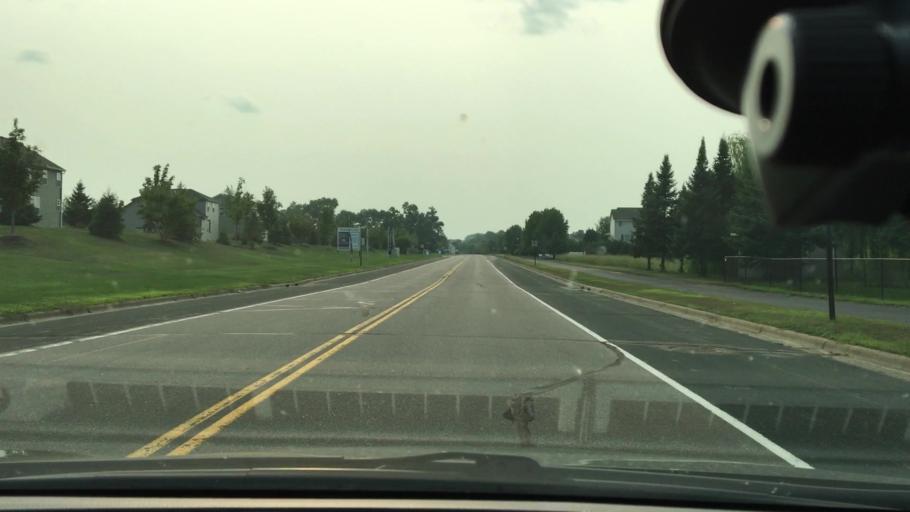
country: US
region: Minnesota
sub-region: Wright County
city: Otsego
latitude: 45.2633
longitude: -93.5690
